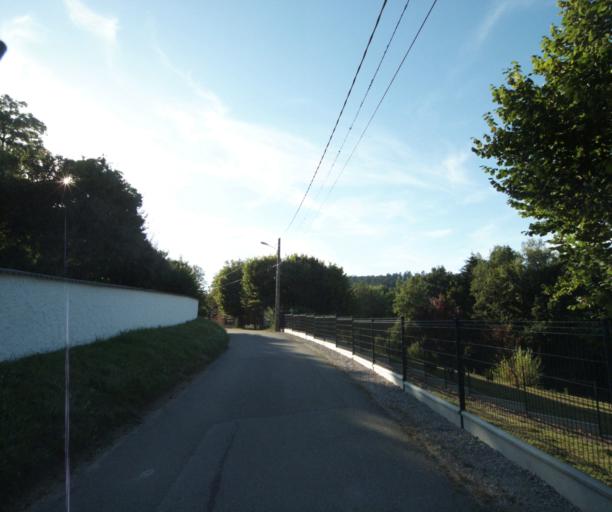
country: FR
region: Lorraine
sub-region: Departement des Vosges
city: Chantraine
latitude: 48.1437
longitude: 6.4393
